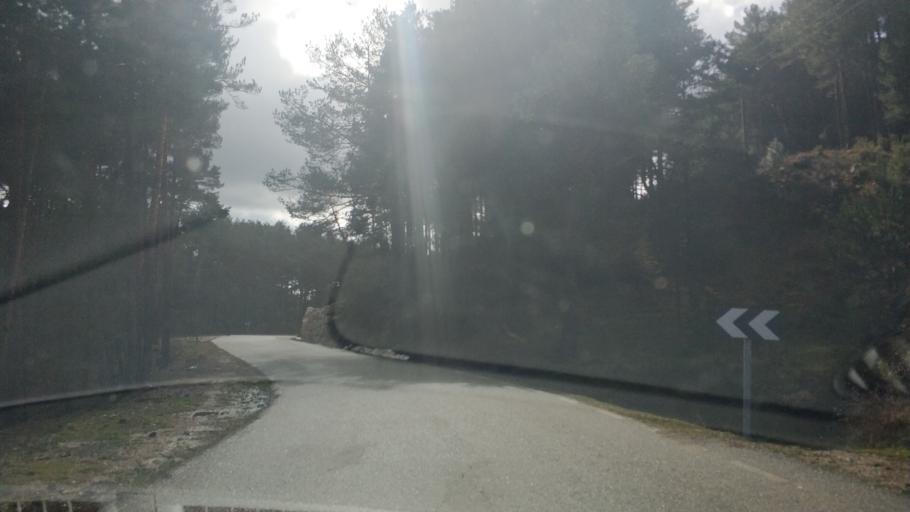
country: ES
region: Castille and Leon
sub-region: Provincia de Burgos
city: Neila
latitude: 42.0243
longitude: -3.0136
